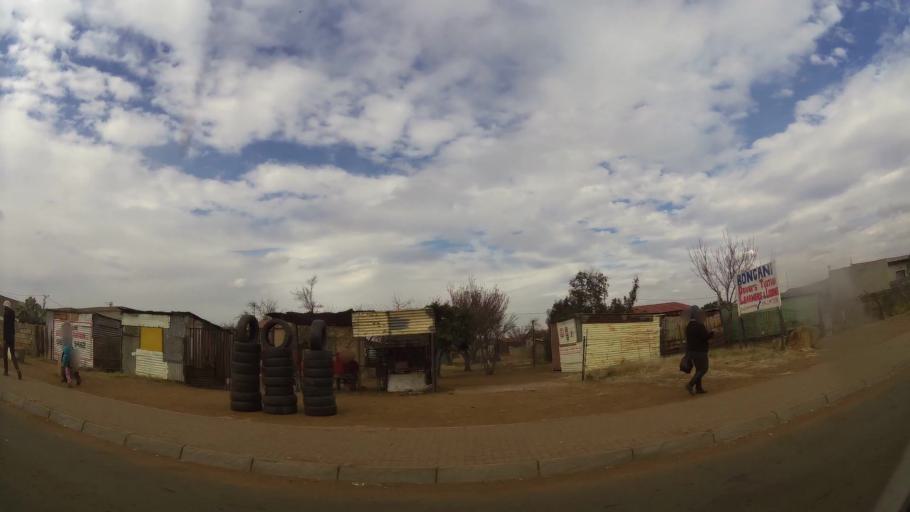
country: ZA
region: Gauteng
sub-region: Ekurhuleni Metropolitan Municipality
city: Germiston
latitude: -26.4019
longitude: 28.1556
